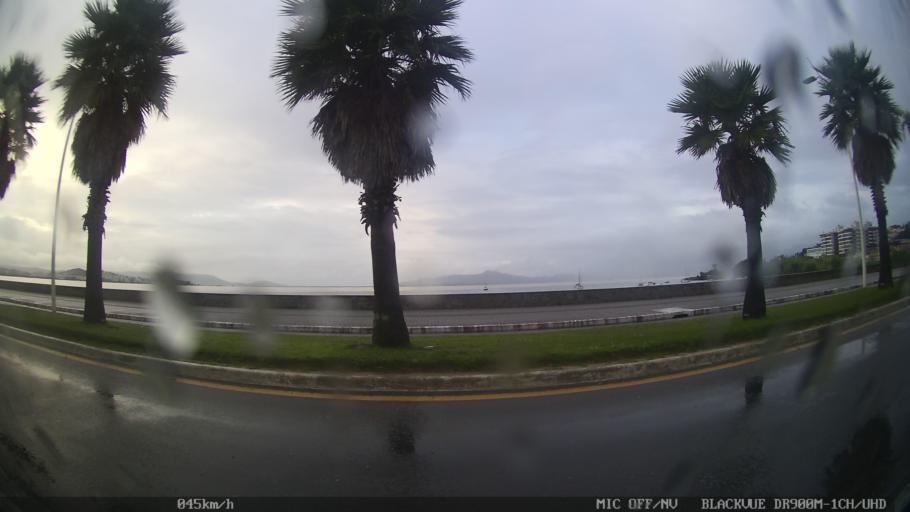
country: BR
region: Santa Catarina
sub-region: Sao Jose
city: Campinas
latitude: -27.6076
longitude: -48.6248
